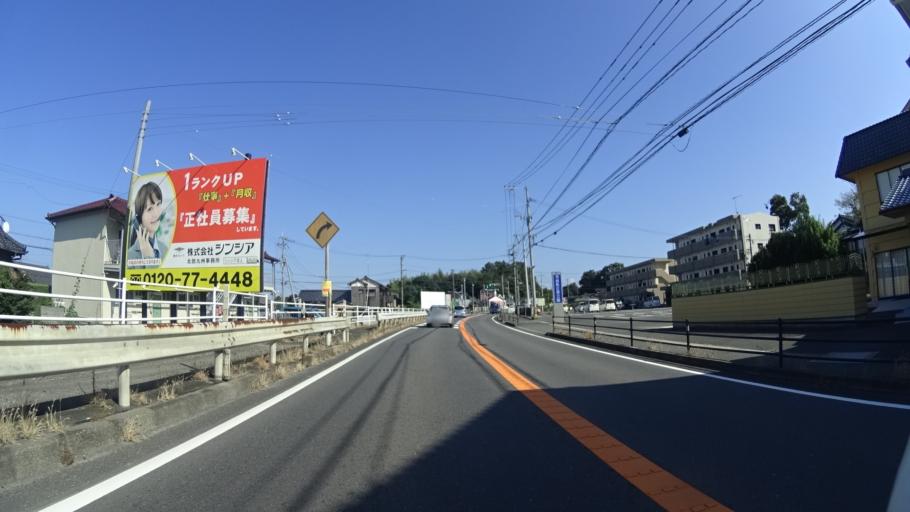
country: JP
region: Fukuoka
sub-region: Buzen-shi
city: Buzen
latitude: 33.6227
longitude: 131.0933
